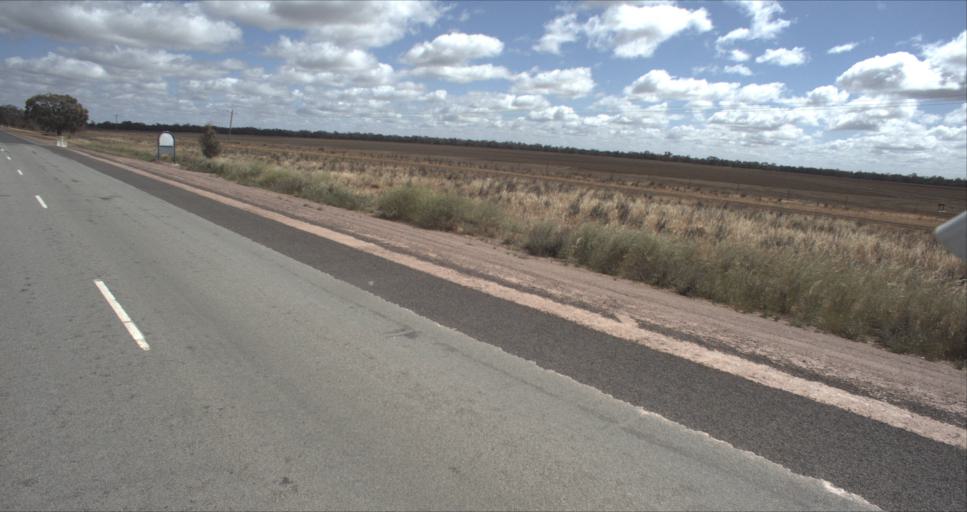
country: AU
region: New South Wales
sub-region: Murrumbidgee Shire
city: Darlington Point
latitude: -34.5664
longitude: 146.0286
